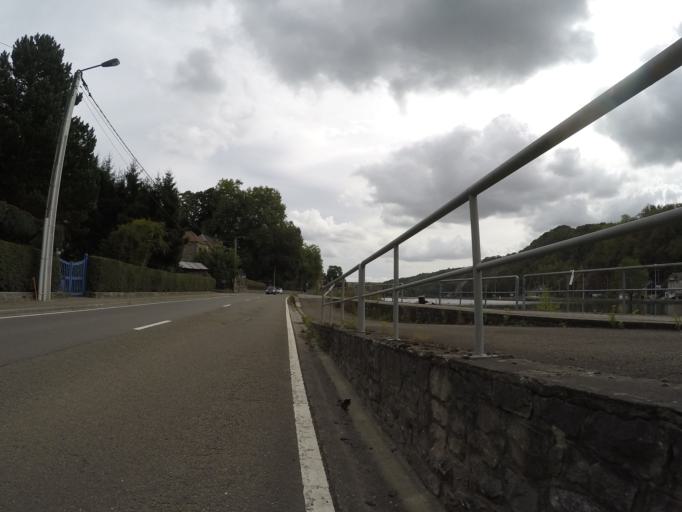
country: BE
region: Wallonia
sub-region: Province de Namur
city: Yvoir
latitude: 50.3360
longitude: 4.8734
